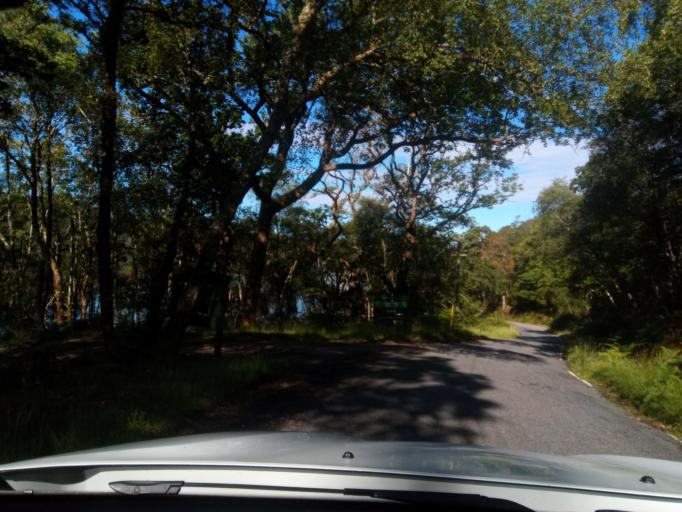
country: GB
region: Scotland
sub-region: Argyll and Bute
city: Isle Of Mull
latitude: 56.6983
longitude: -5.6894
